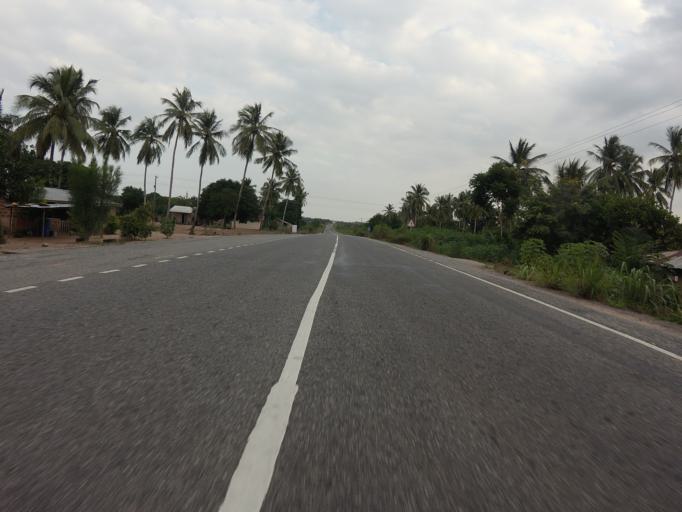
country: GH
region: Volta
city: Ho
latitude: 6.2492
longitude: 0.5507
